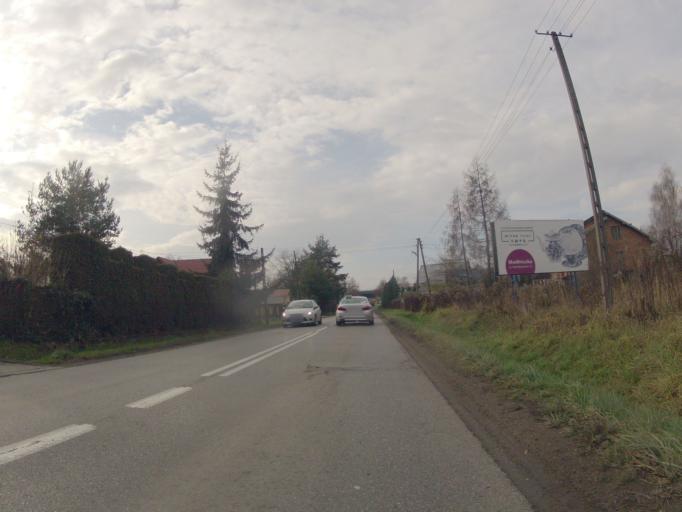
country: PL
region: Lesser Poland Voivodeship
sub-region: Powiat krakowski
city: Balice
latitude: 50.0863
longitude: 19.8118
